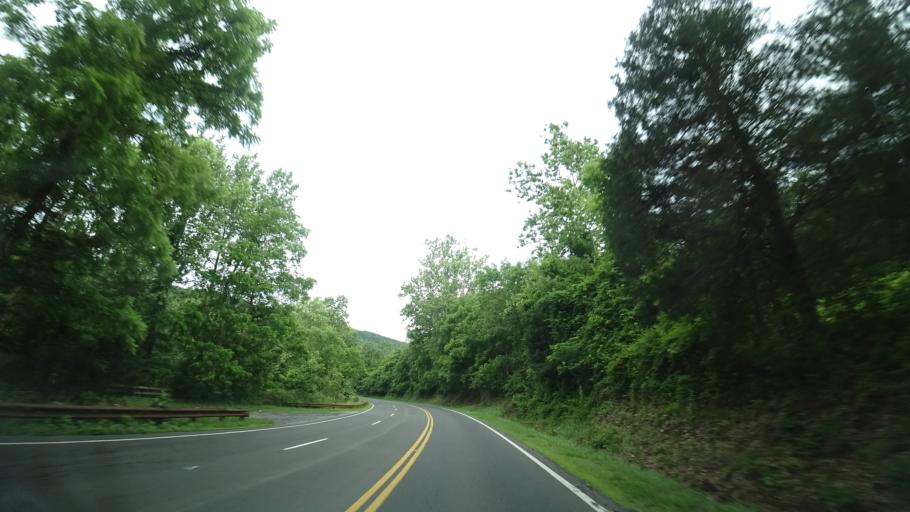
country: US
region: Virginia
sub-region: Page County
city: Luray
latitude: 38.6583
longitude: -78.3660
